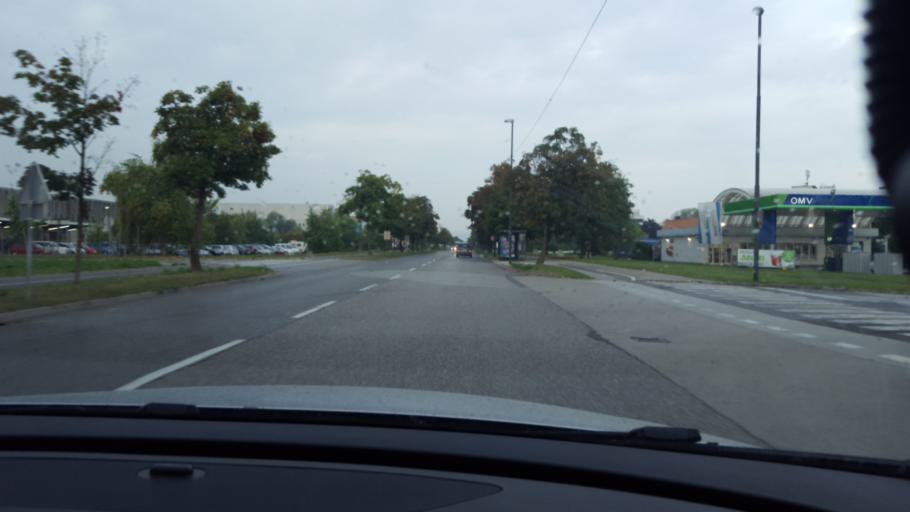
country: SI
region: Dol pri Ljubljani
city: Dol pri Ljubljani
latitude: 46.0622
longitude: 14.5713
